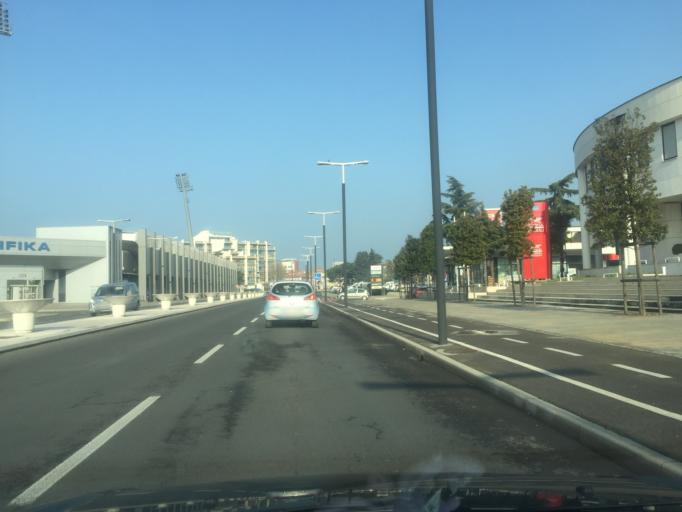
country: SI
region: Koper-Capodistria
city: Koper
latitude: 45.5416
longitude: 13.7321
